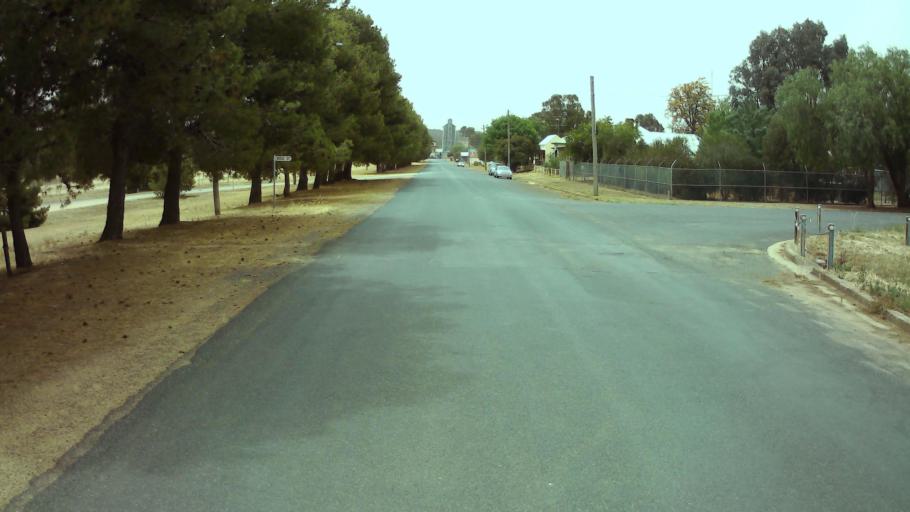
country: AU
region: New South Wales
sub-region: Weddin
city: Grenfell
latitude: -33.8995
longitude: 148.1554
